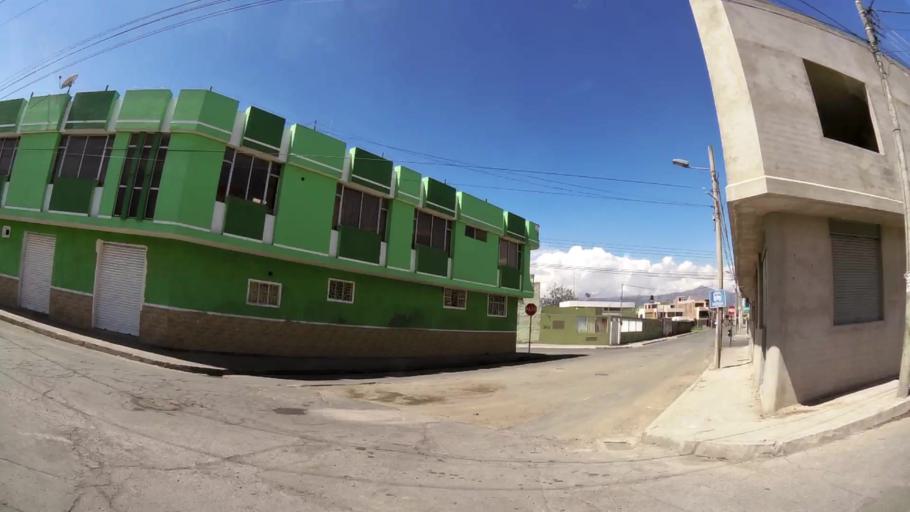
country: EC
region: Chimborazo
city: Riobamba
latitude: -1.6712
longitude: -78.6401
